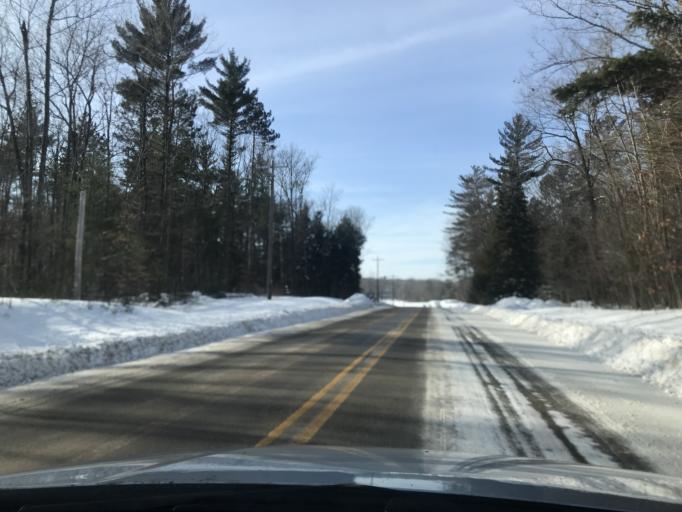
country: US
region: Wisconsin
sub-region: Oconto County
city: Oconto Falls
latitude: 45.1477
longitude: -88.1852
